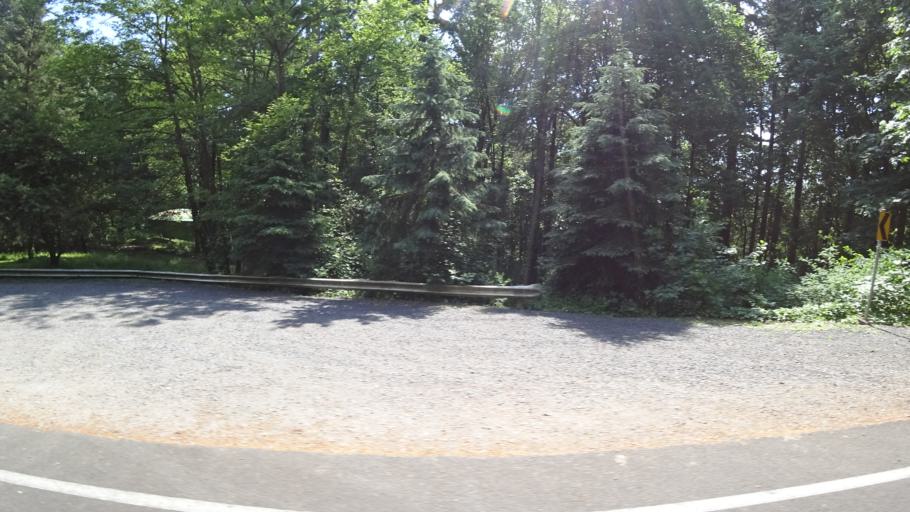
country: US
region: Oregon
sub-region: Multnomah County
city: Portland
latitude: 45.5130
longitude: -122.7051
